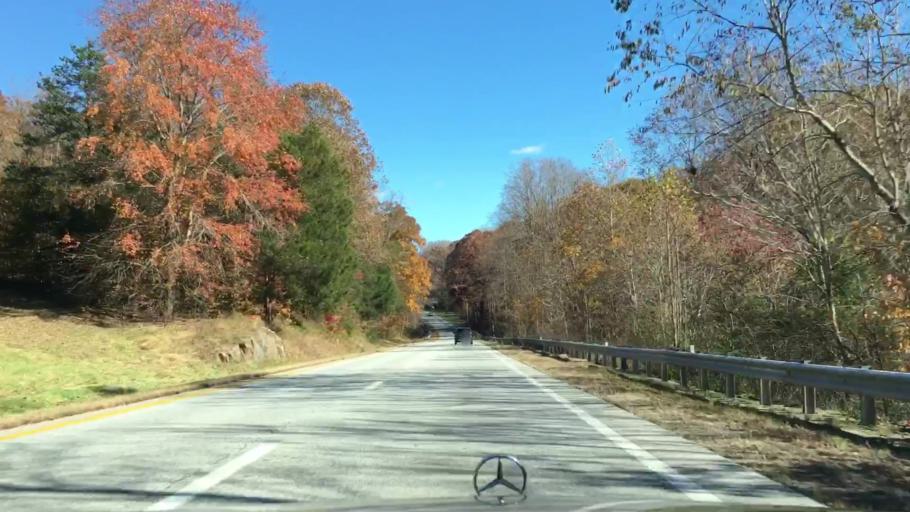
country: US
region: Virginia
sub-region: Nelson County
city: Nellysford
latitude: 37.8427
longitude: -78.7814
